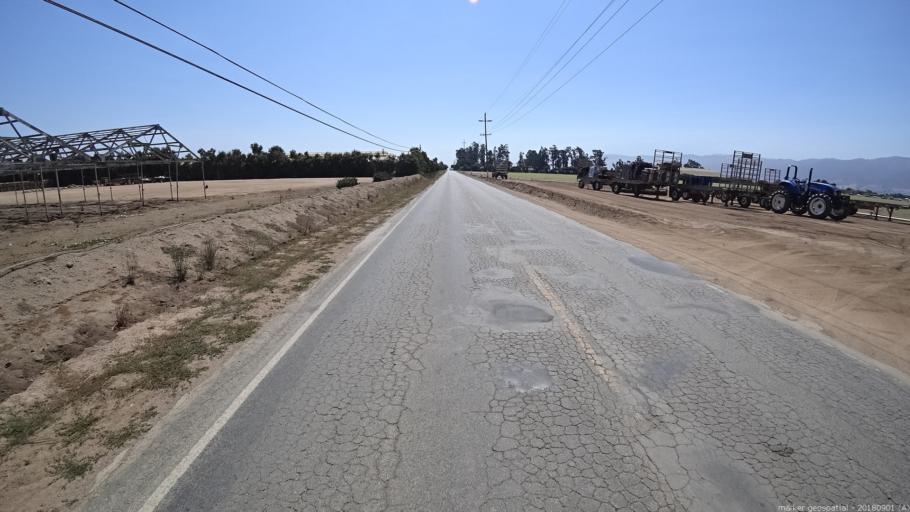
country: US
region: California
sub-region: Monterey County
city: Chualar
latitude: 36.6213
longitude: -121.5263
